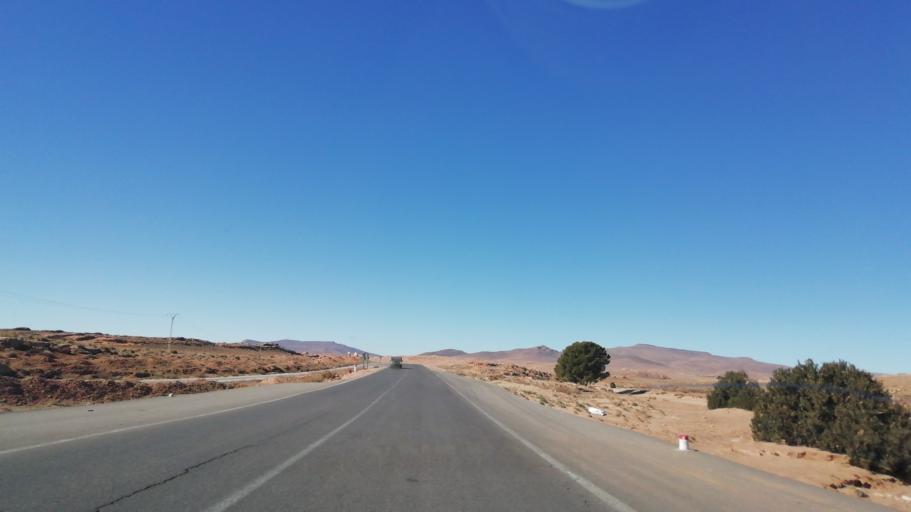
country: DZ
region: El Bayadh
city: El Bayadh
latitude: 33.6144
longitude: 1.2165
